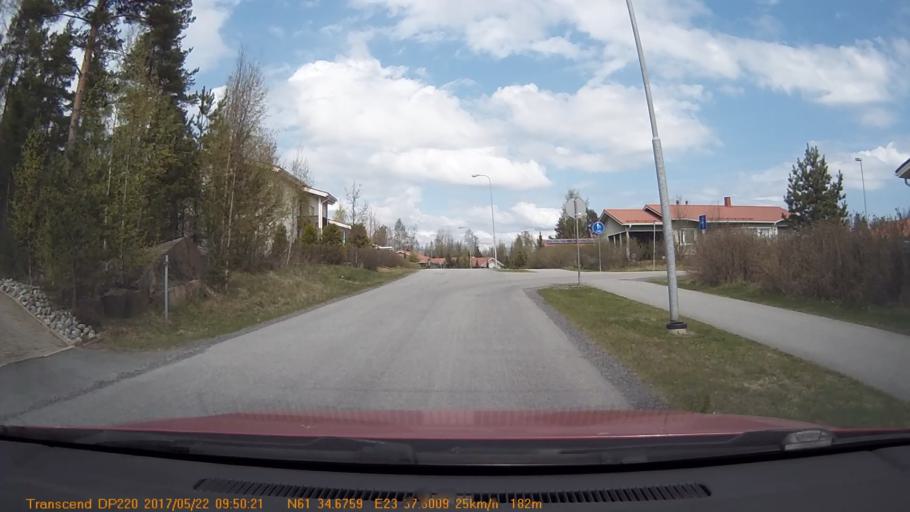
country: FI
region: Pirkanmaa
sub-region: Tampere
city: Yloejaervi
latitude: 61.5779
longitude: 23.6264
